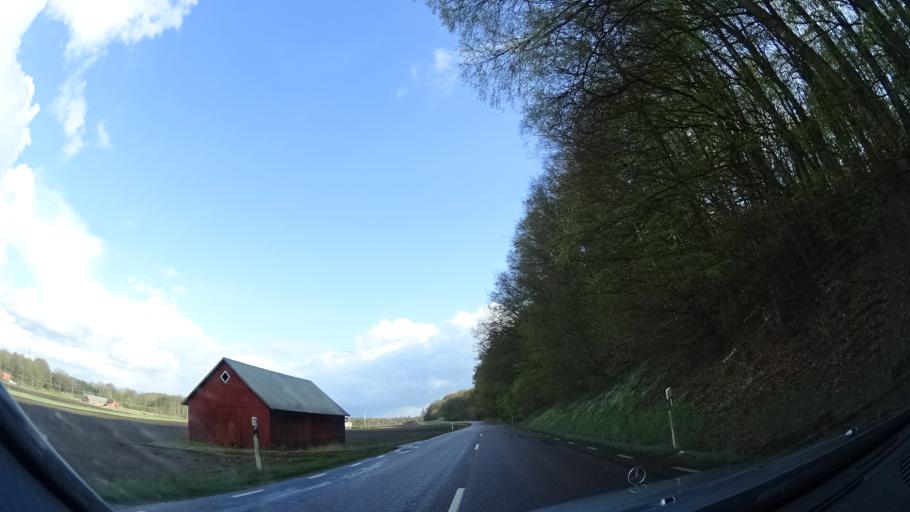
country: SE
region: Skane
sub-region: Klippans Kommun
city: Ljungbyhed
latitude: 56.0322
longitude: 13.2619
